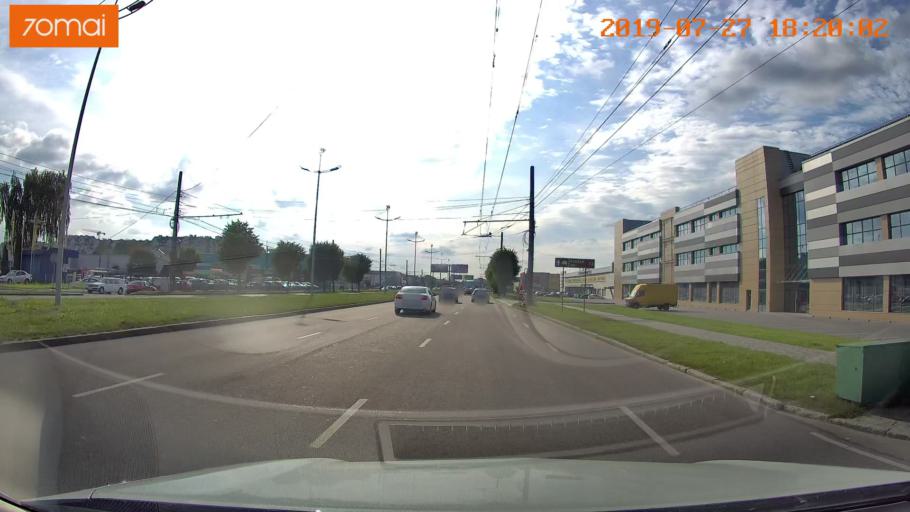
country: RU
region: Kaliningrad
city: Bol'shoe Isakovo
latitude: 54.7074
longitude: 20.5812
